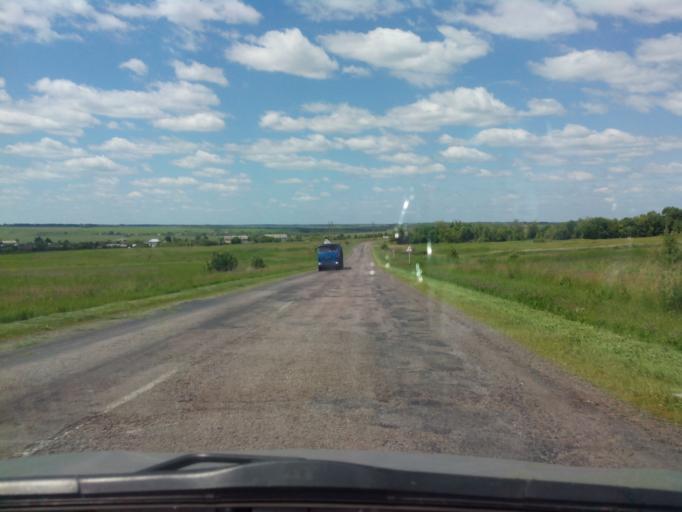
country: RU
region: Voronezj
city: Ternovka
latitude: 51.5933
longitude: 41.8016
